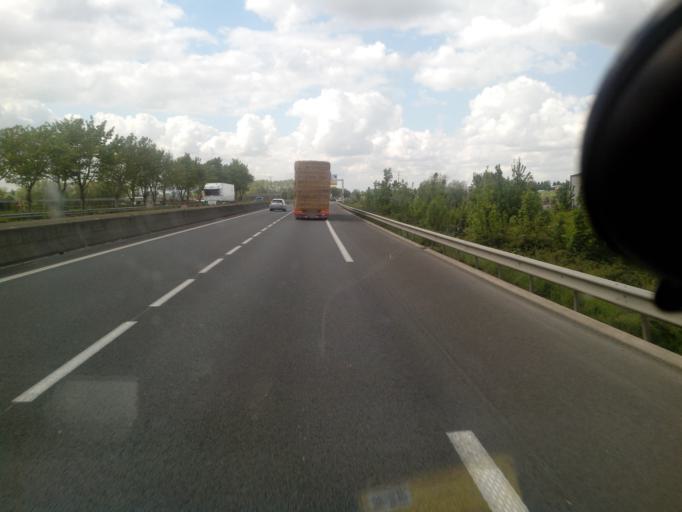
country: FR
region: Nord-Pas-de-Calais
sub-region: Departement du Nord
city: Meteren
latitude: 50.7356
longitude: 2.6917
